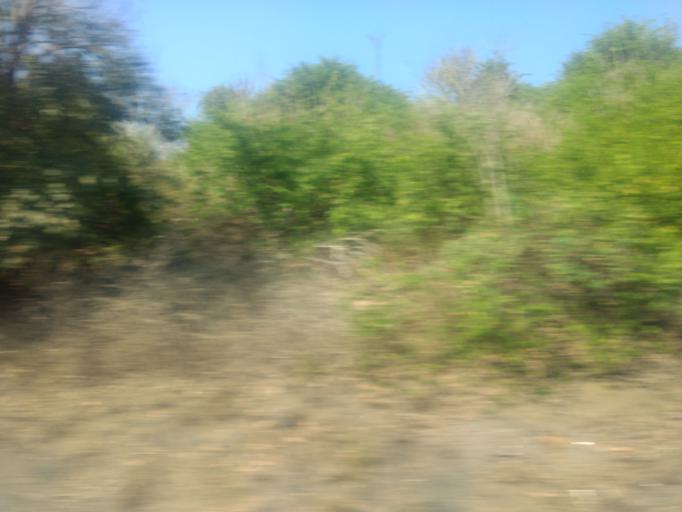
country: MX
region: Colima
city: Armeria
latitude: 18.9435
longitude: -104.1102
